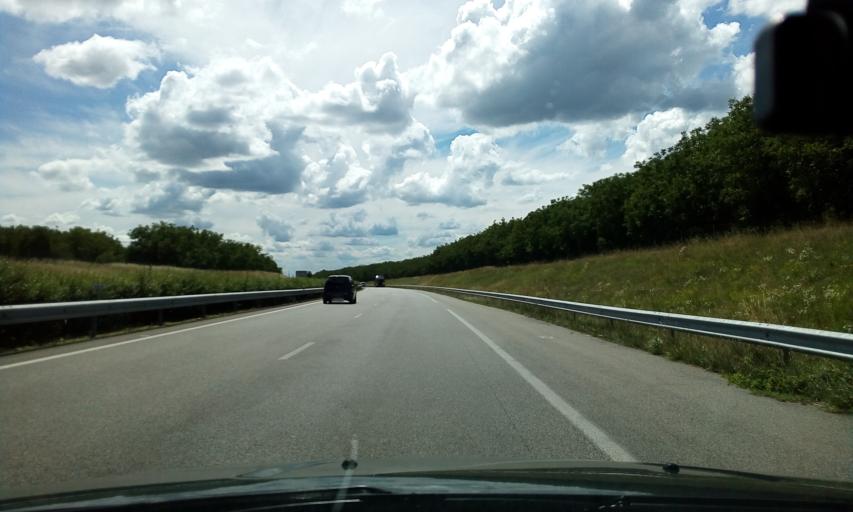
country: FR
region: Rhone-Alpes
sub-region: Departement de l'Isere
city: Saint-Romans
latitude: 45.1319
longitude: 5.3114
